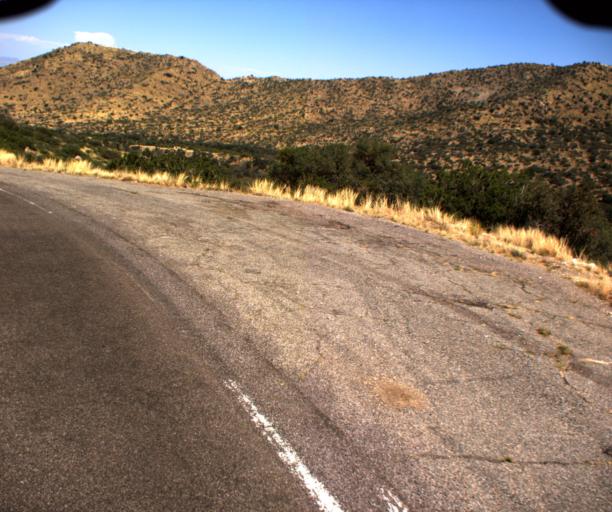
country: US
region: Arizona
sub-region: Graham County
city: Swift Trail Junction
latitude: 32.6718
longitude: -109.7857
